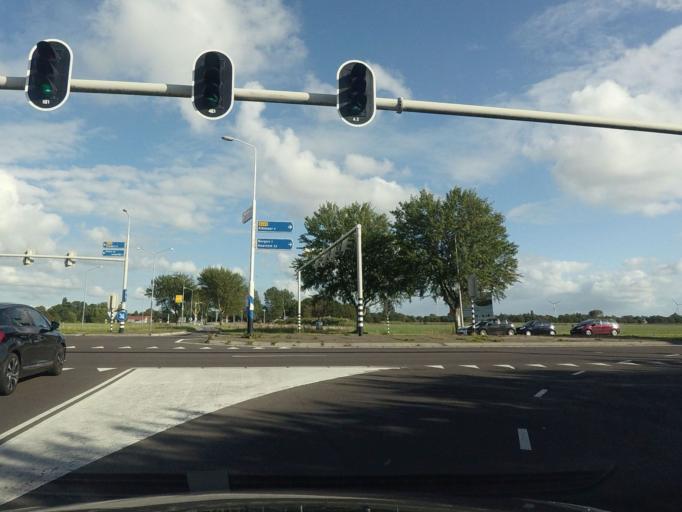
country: NL
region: North Holland
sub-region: Gemeente Langedijk
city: Broek op Langedijk
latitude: 52.6651
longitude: 4.7736
